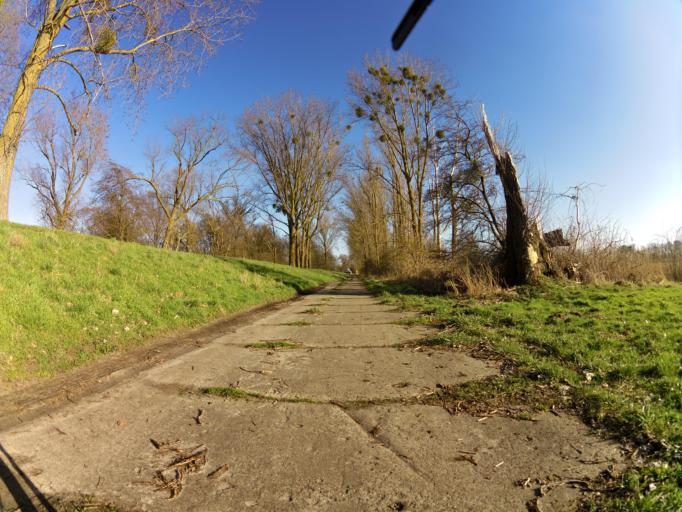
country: PL
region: West Pomeranian Voivodeship
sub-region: Powiat policki
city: Nowe Warpno
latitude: 53.7008
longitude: 14.3641
